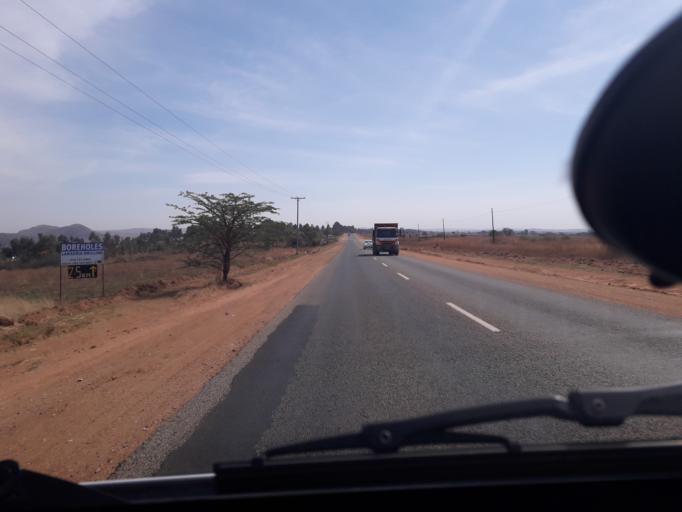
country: ZA
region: Gauteng
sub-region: West Rand District Municipality
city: Muldersdriseloop
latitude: -26.0072
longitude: 27.8582
